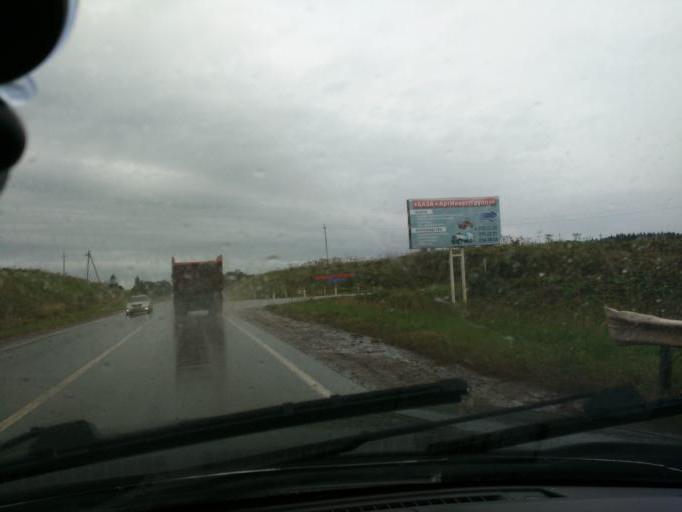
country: RU
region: Perm
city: Kultayevo
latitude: 57.8527
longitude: 55.8500
